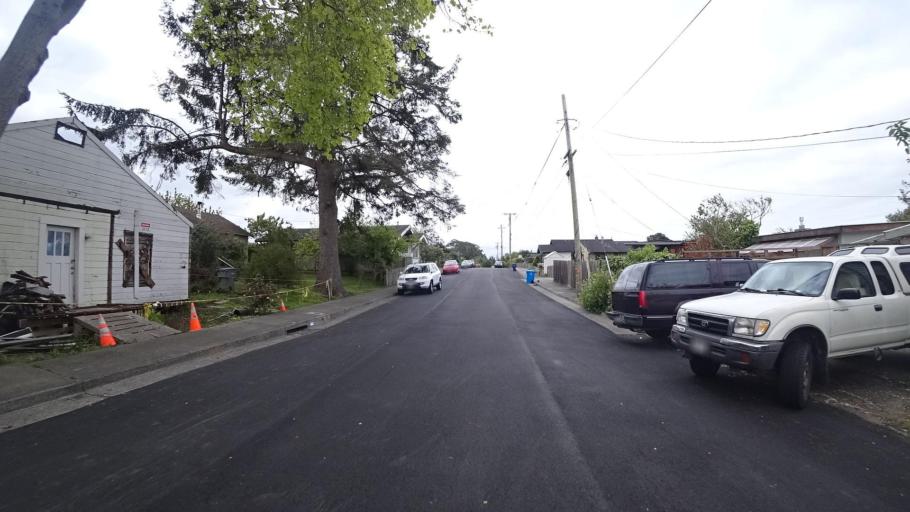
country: US
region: California
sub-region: Humboldt County
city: Arcata
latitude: 40.8815
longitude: -124.0912
